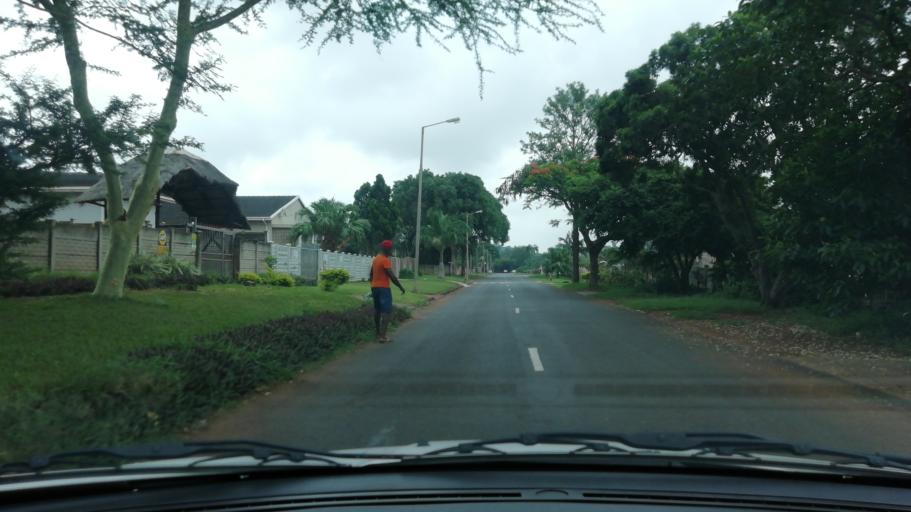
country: ZA
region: KwaZulu-Natal
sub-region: uThungulu District Municipality
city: Empangeni
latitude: -28.7622
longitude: 31.8992
